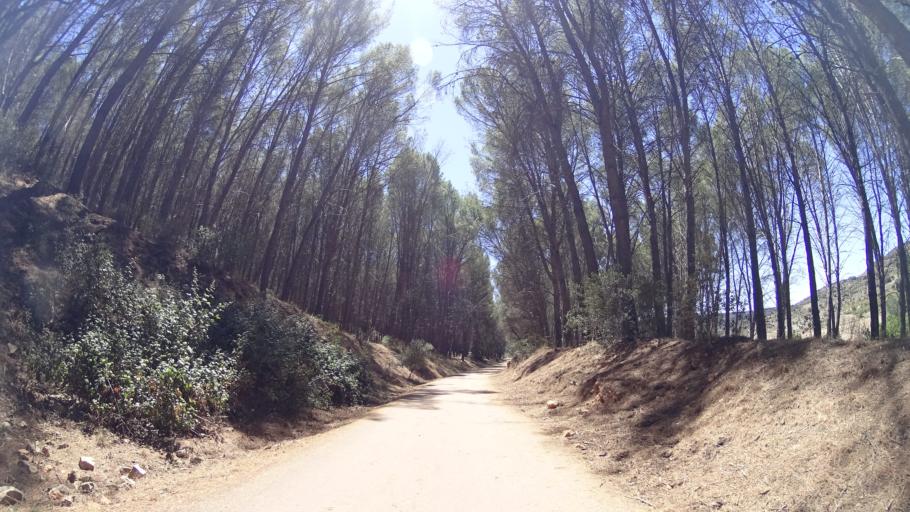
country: ES
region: Madrid
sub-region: Provincia de Madrid
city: Ambite
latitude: 40.3237
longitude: -3.1796
